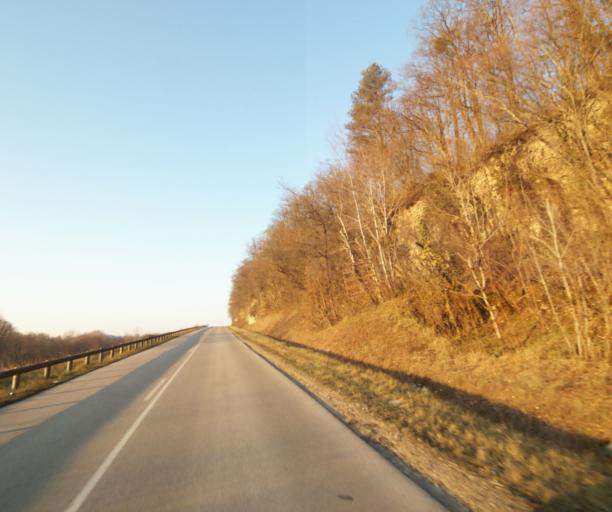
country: FR
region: Champagne-Ardenne
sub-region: Departement de la Haute-Marne
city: Bienville
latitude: 48.5883
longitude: 5.0436
